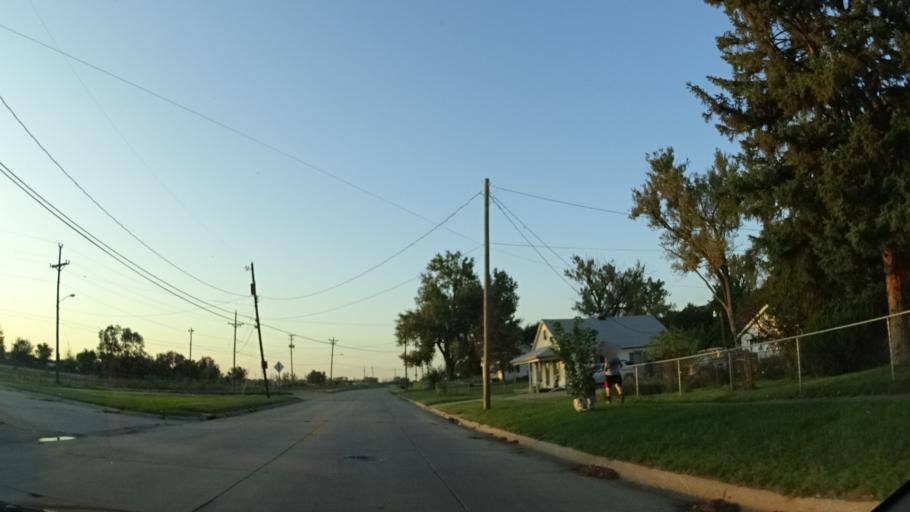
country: US
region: Iowa
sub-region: Pottawattamie County
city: Council Bluffs
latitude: 41.2741
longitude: -95.8585
